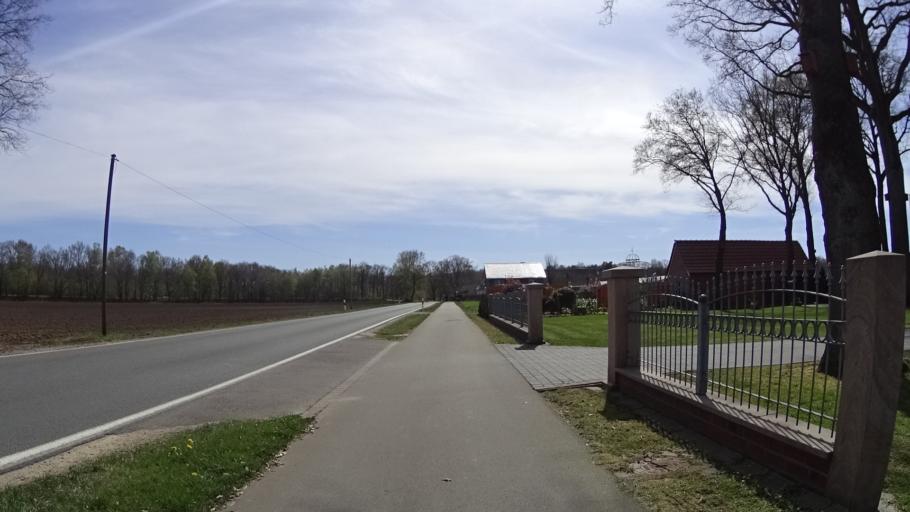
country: DE
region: Lower Saxony
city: Spelle
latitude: 52.3324
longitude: 7.4534
